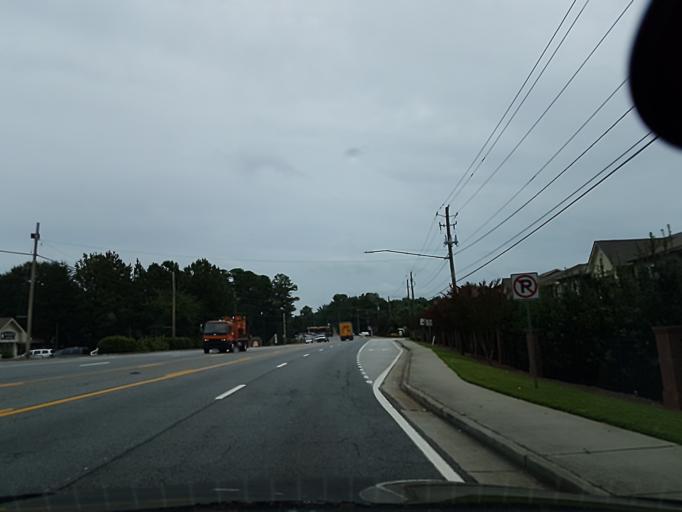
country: US
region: Georgia
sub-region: DeKalb County
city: Scottdale
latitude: 33.8182
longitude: -84.2670
